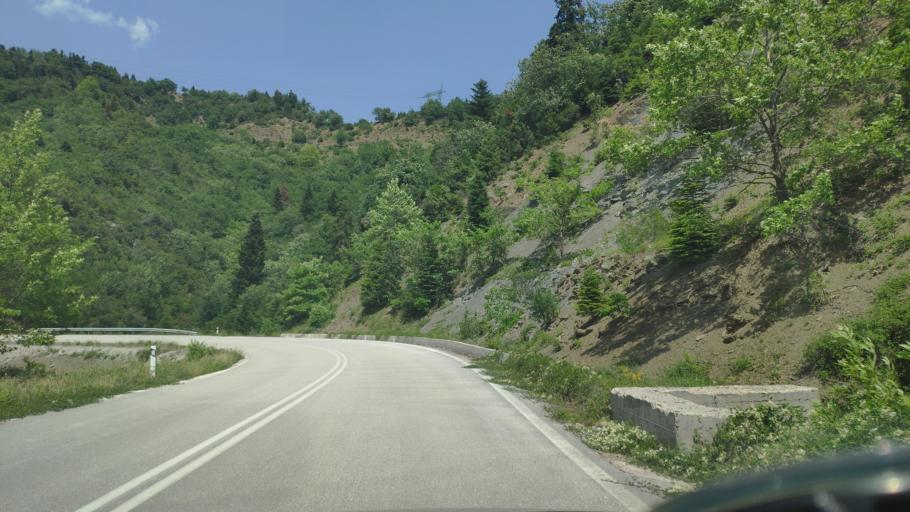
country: GR
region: Epirus
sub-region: Nomos Artas
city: Ano Kalentini
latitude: 39.2732
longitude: 21.3304
